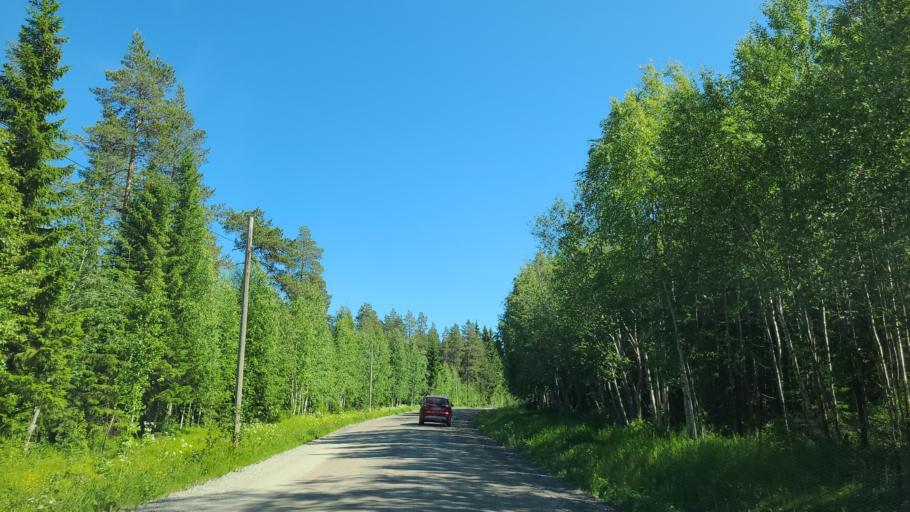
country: SE
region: Vaesterbotten
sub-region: Bjurholms Kommun
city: Bjurholm
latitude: 63.6848
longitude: 18.9703
